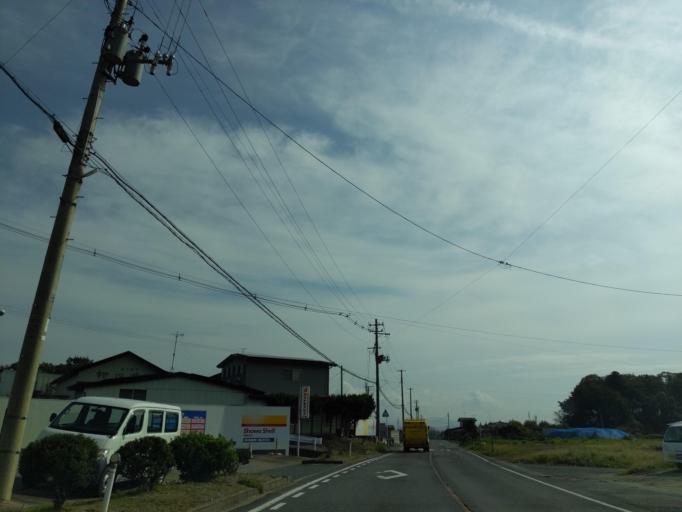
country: JP
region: Fukushima
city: Koriyama
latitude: 37.4202
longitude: 140.3185
